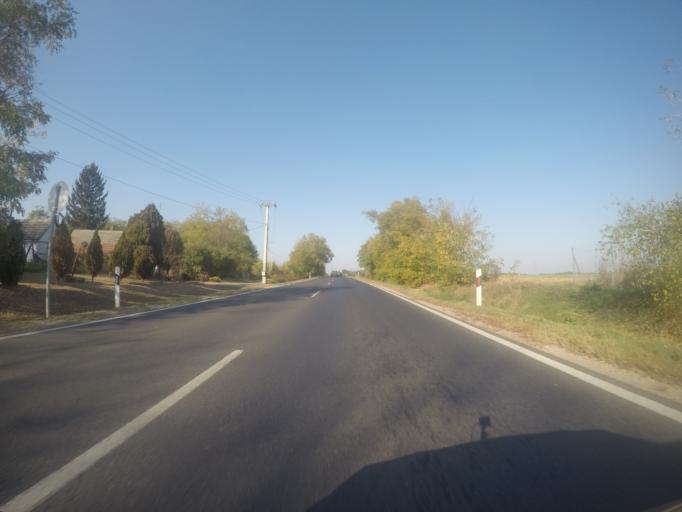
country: HU
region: Tolna
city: Dunafoldvar
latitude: 46.8380
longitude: 18.9099
